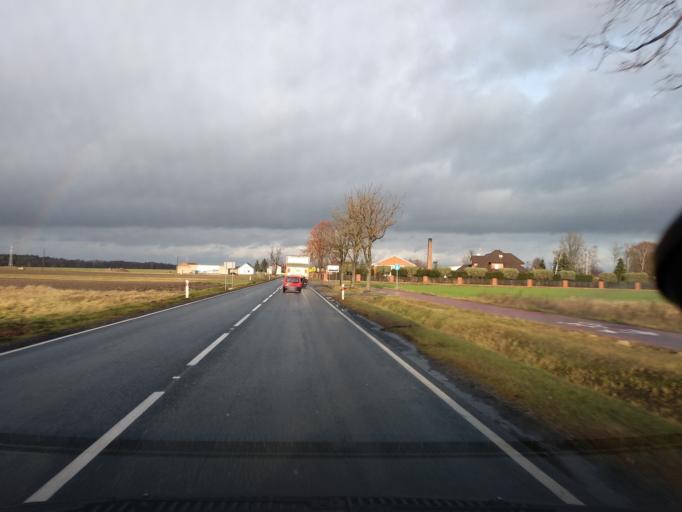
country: PL
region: Greater Poland Voivodeship
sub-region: Powiat koninski
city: Rychwal
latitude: 52.1133
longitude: 18.1676
